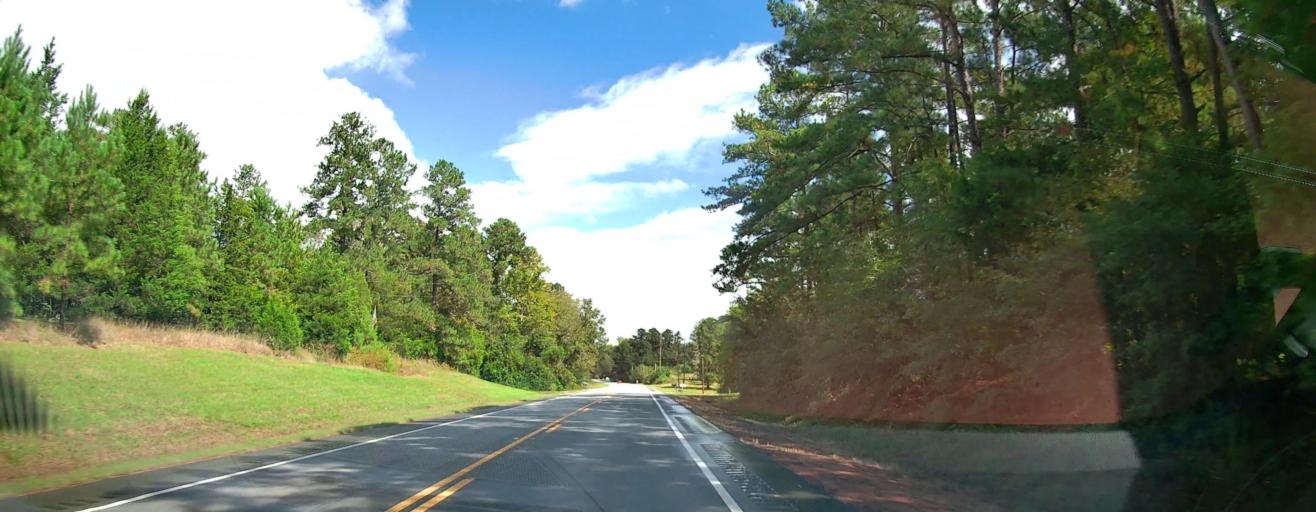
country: US
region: Georgia
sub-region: Baldwin County
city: Milledgeville
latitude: 33.0309
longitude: -83.3200
